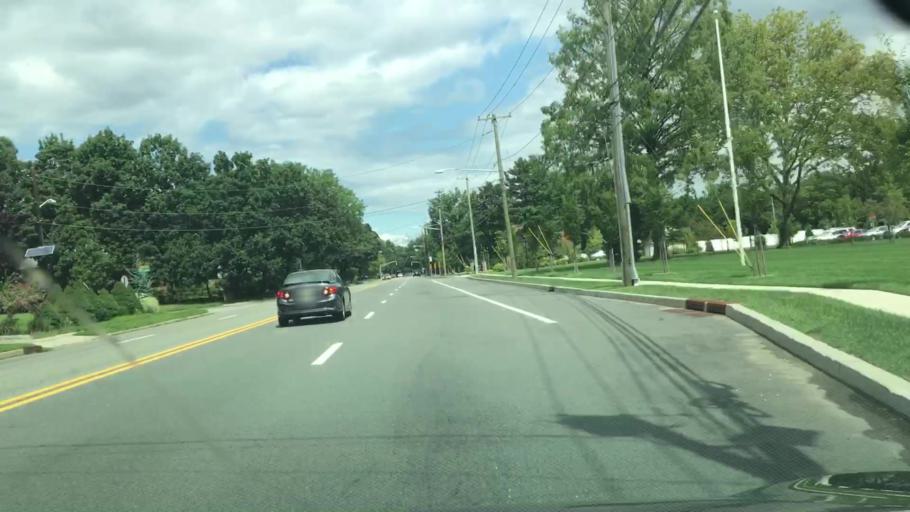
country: US
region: New Jersey
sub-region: Bergen County
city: River Edge
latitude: 40.9423
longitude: -74.0512
